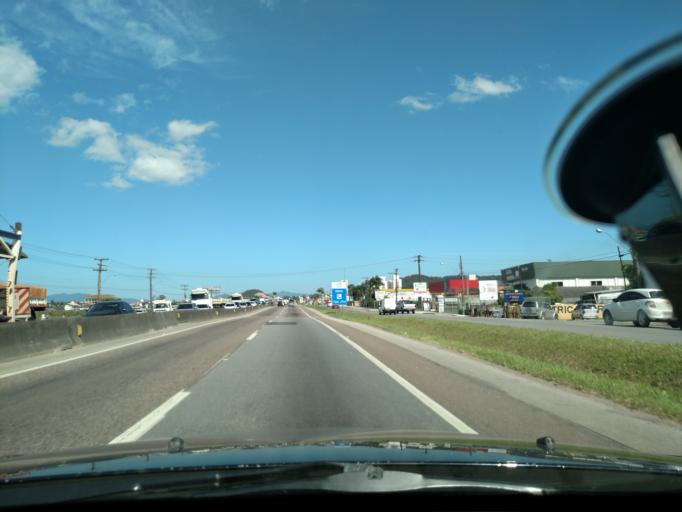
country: BR
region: Santa Catarina
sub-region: Biguacu
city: Biguacu
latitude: -27.5025
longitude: -48.6525
